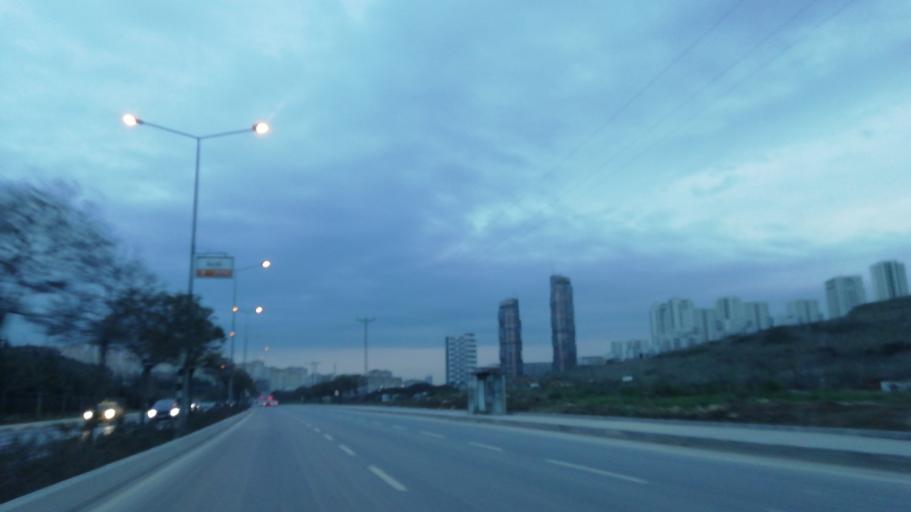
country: TR
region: Istanbul
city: Mahmutbey
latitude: 41.0488
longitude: 28.7741
